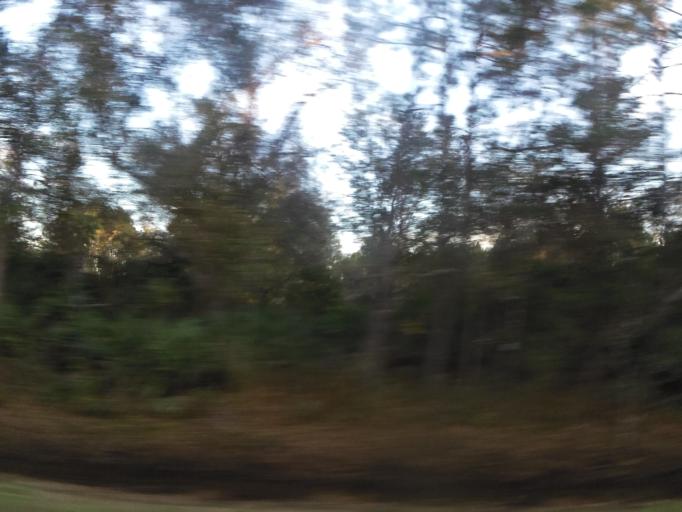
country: US
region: Florida
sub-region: Clay County
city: Green Cove Springs
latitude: 29.9503
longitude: -81.5531
